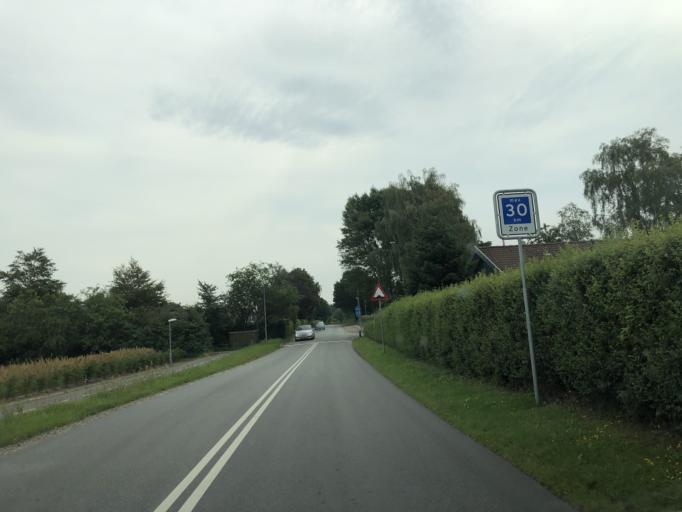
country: DK
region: Central Jutland
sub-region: Viborg Kommune
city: Stoholm
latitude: 56.4486
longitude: 9.1818
